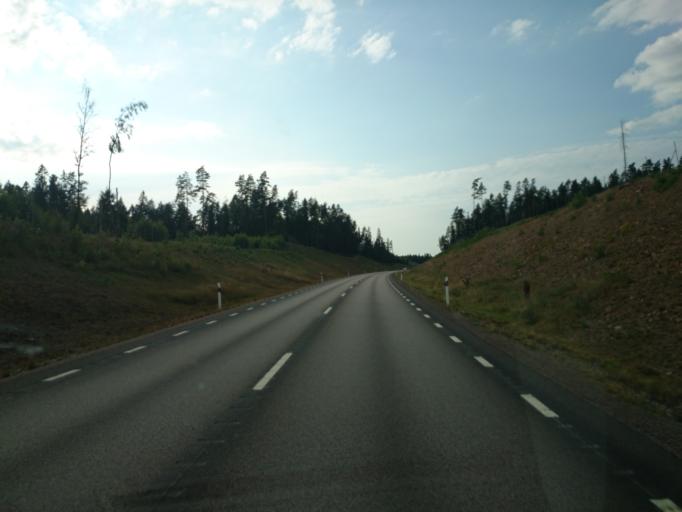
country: SE
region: Skane
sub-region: Osby Kommun
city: Osby
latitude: 56.4240
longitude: 13.8864
